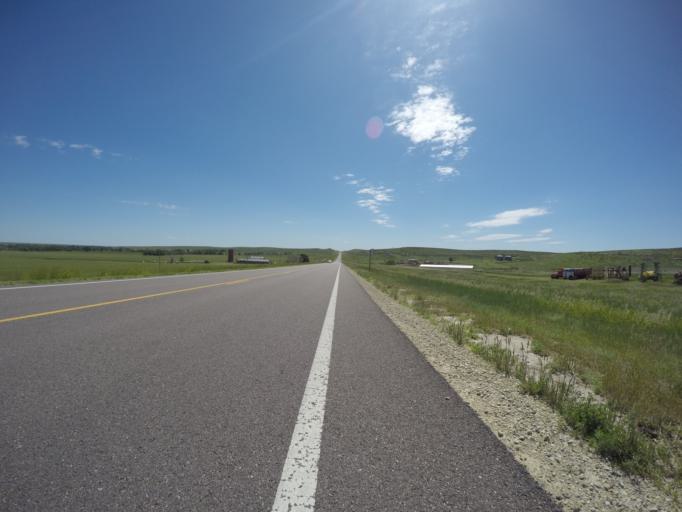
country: US
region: Kansas
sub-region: Rawlins County
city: Atwood
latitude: 39.8133
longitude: -101.0167
